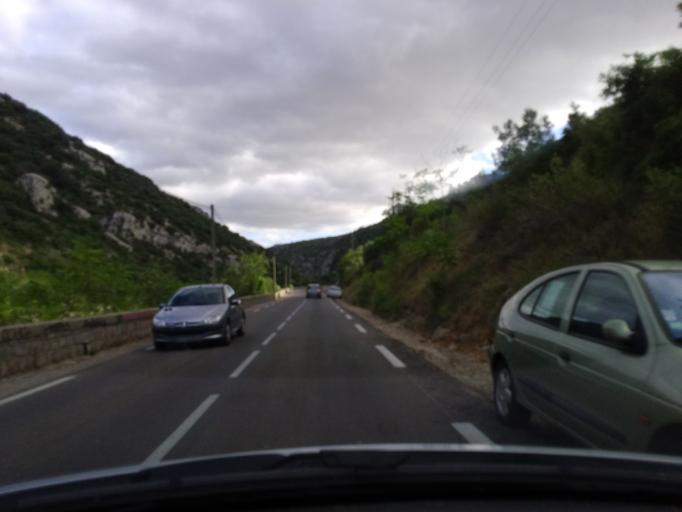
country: FR
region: Languedoc-Roussillon
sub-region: Departement de l'Herault
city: Saint-Jean-de-Fos
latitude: 43.7198
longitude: 3.5534
